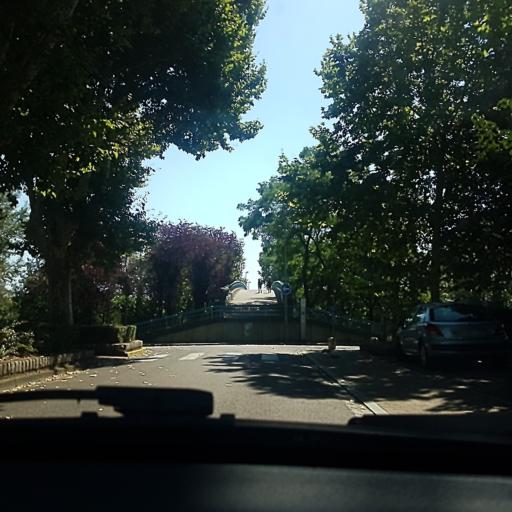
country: FR
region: Bourgogne
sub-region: Departement de Saone-et-Loire
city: Chalon-sur-Saone
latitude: 46.7780
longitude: 4.8603
